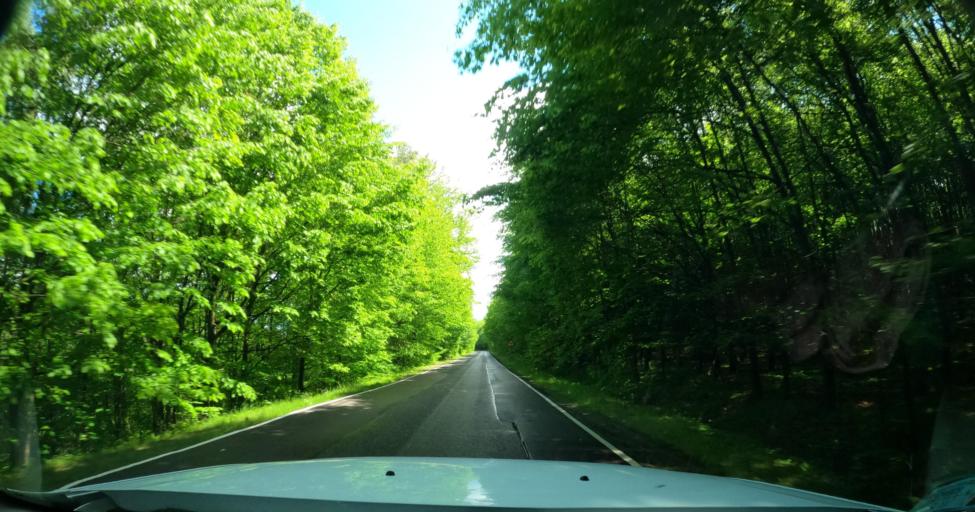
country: PL
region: Pomeranian Voivodeship
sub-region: Powiat bytowski
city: Czarna Dabrowka
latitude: 54.3777
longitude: 17.4930
